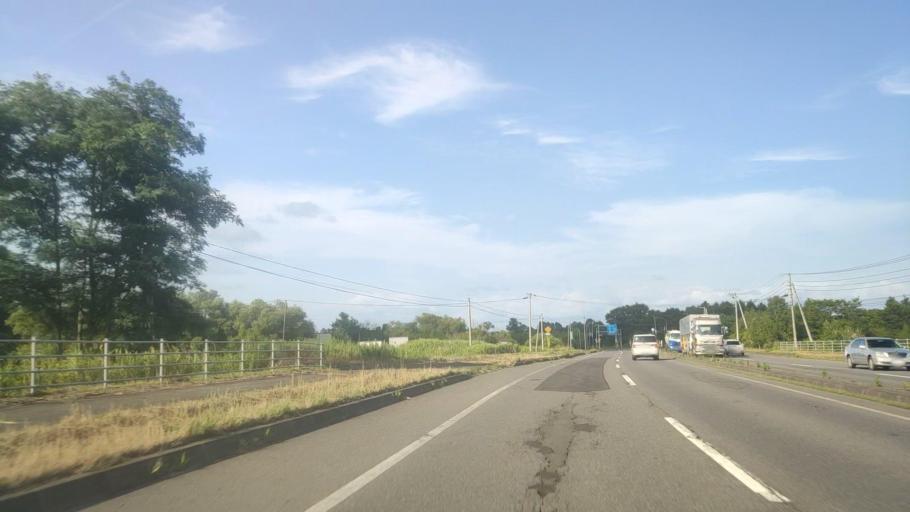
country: JP
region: Hokkaido
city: Chitose
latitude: 42.7757
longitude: 141.8283
